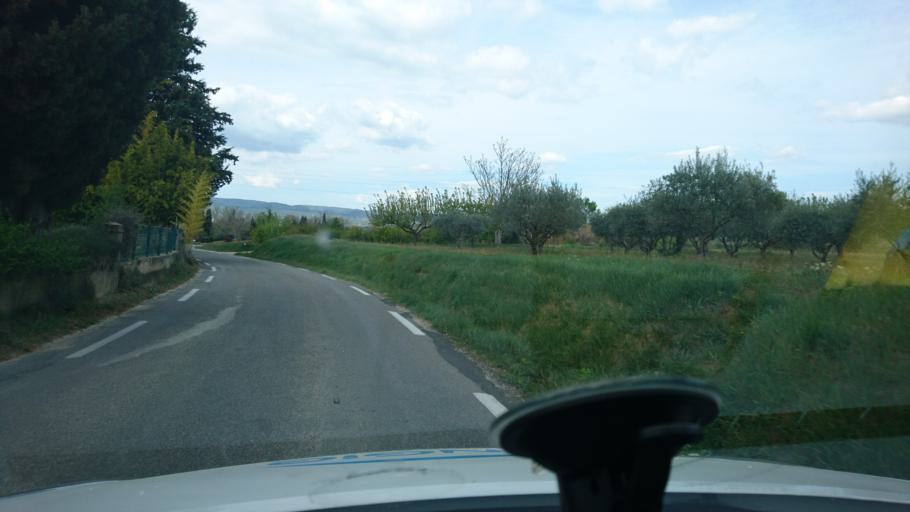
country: FR
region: Provence-Alpes-Cote d'Azur
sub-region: Departement du Vaucluse
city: Maubec
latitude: 43.8555
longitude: 5.1623
